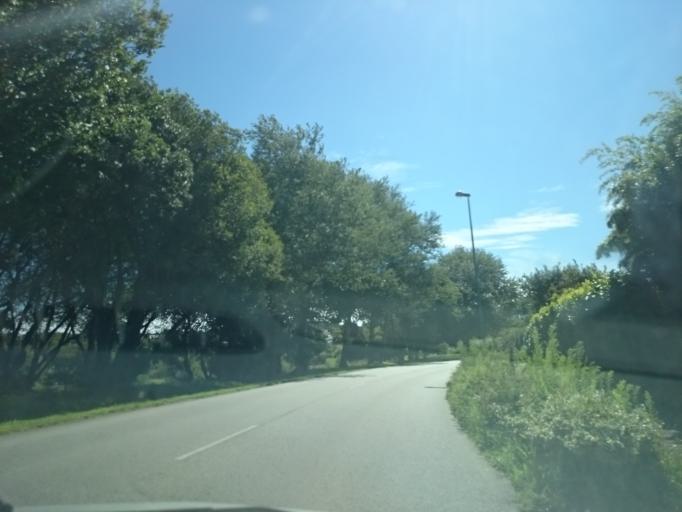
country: FR
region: Brittany
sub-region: Departement du Finistere
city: Saint-Renan
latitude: 48.4366
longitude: -4.6235
